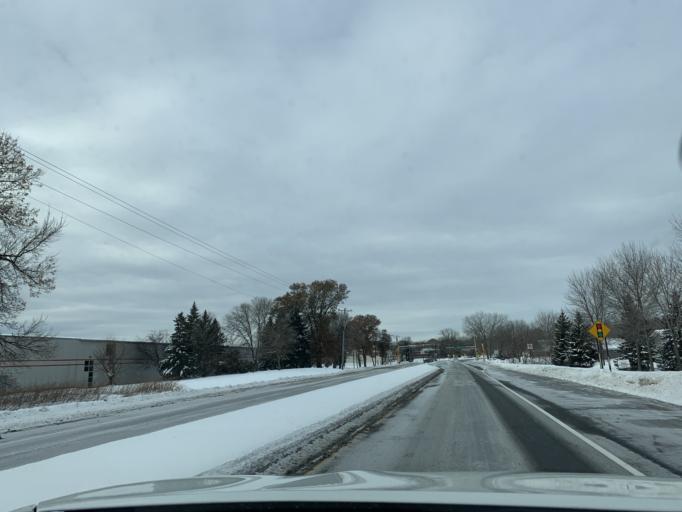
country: US
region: Minnesota
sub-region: Anoka County
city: Andover
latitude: 45.1813
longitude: -93.2953
